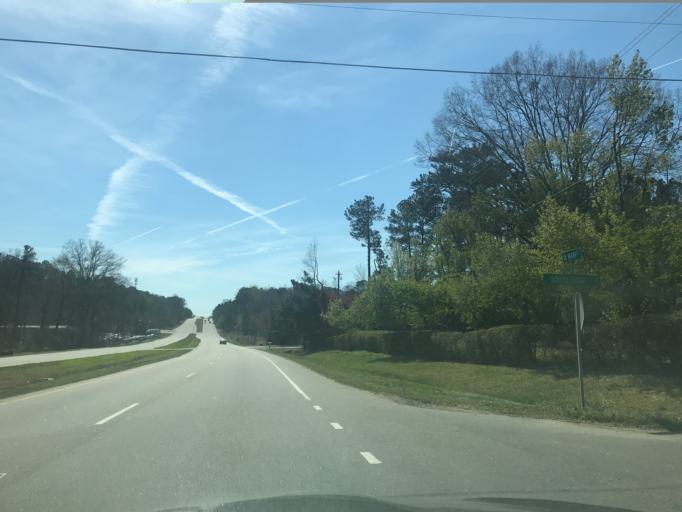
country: US
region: North Carolina
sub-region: Wake County
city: Fuquay-Varina
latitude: 35.6173
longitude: -78.7340
